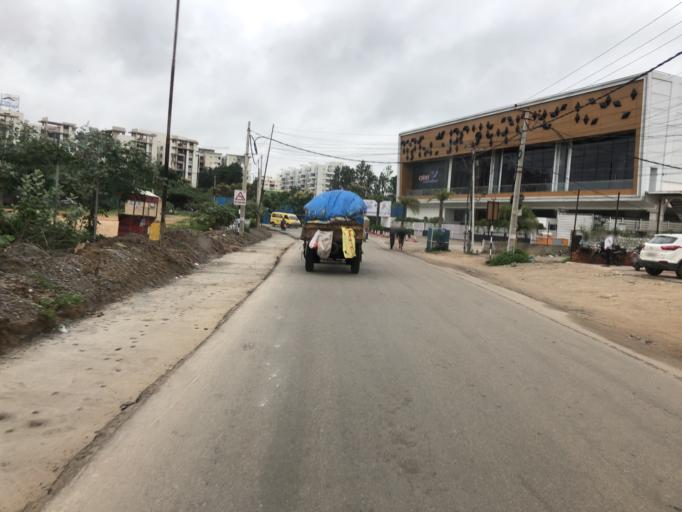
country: IN
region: Telangana
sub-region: Rangareddi
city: Kukatpalli
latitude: 17.4654
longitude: 78.3735
